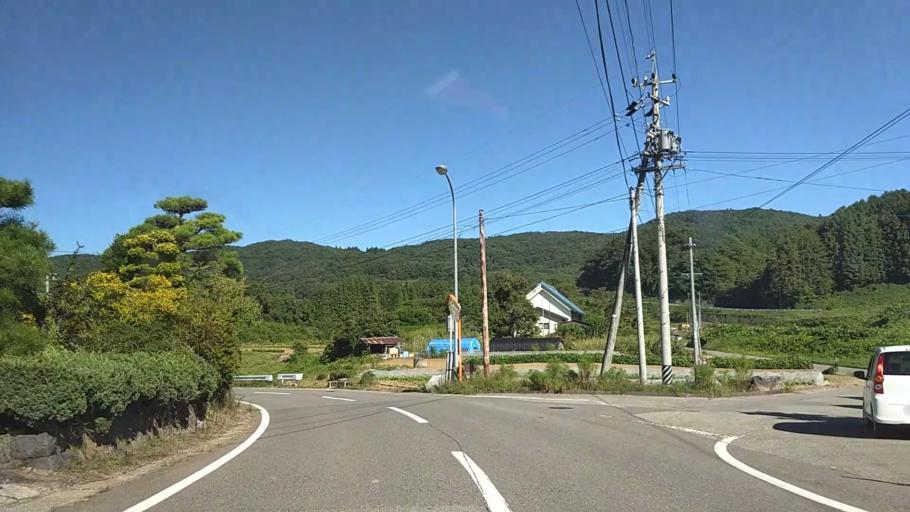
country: JP
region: Nagano
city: Nagano-shi
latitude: 36.6006
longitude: 138.0920
